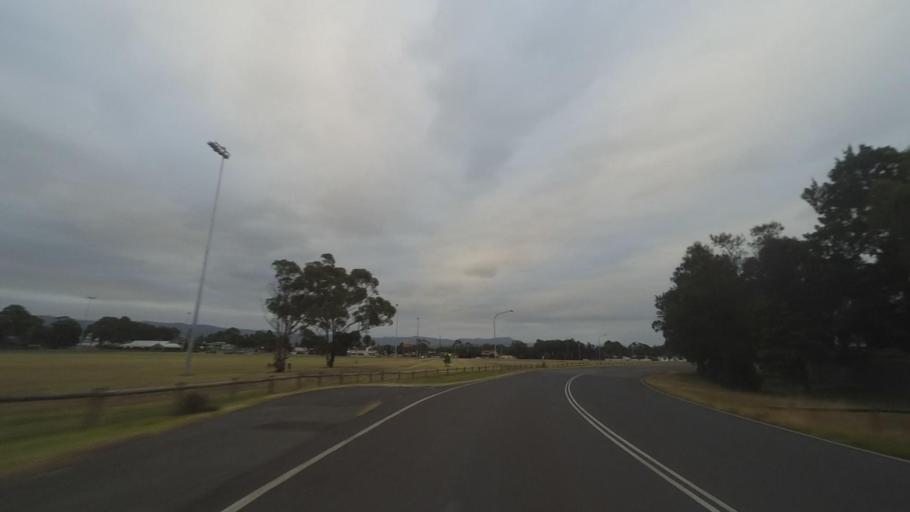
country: AU
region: New South Wales
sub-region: Shellharbour
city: Albion Park Rail
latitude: -34.5712
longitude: 150.8039
